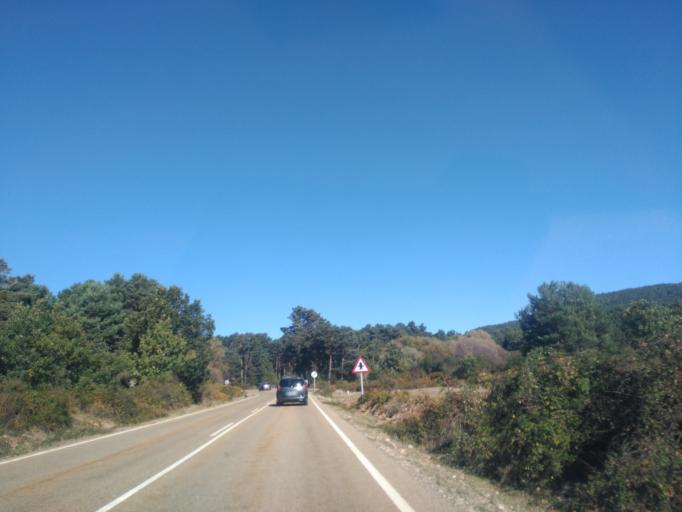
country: ES
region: Castille and Leon
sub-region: Provincia de Soria
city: Vinuesa
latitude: 41.9660
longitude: -2.7812
